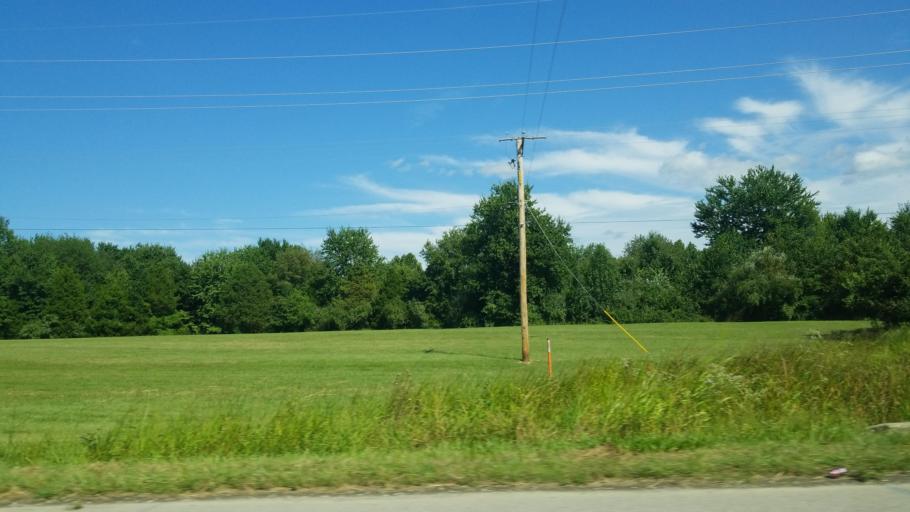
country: US
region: Illinois
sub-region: Williamson County
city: Marion
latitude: 37.7545
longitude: -88.9327
